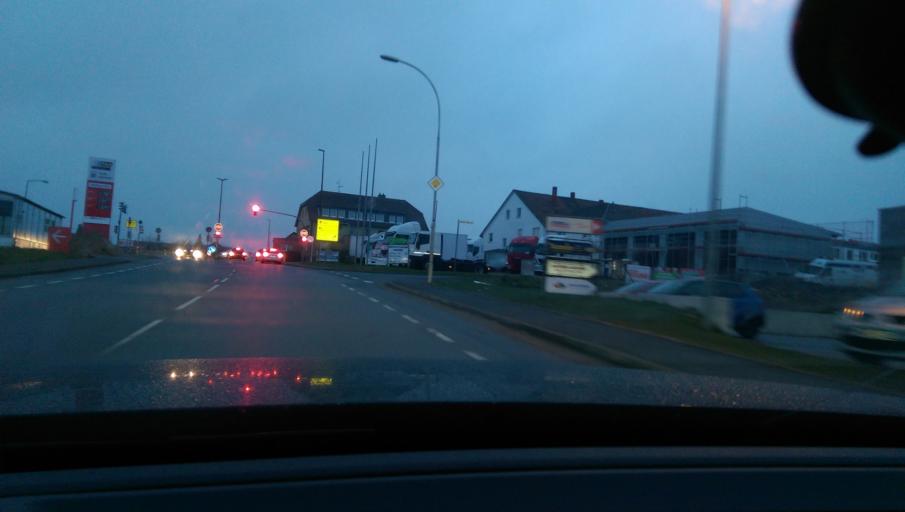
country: DE
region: Lower Saxony
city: Wennigsen
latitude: 52.2818
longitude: 9.5745
